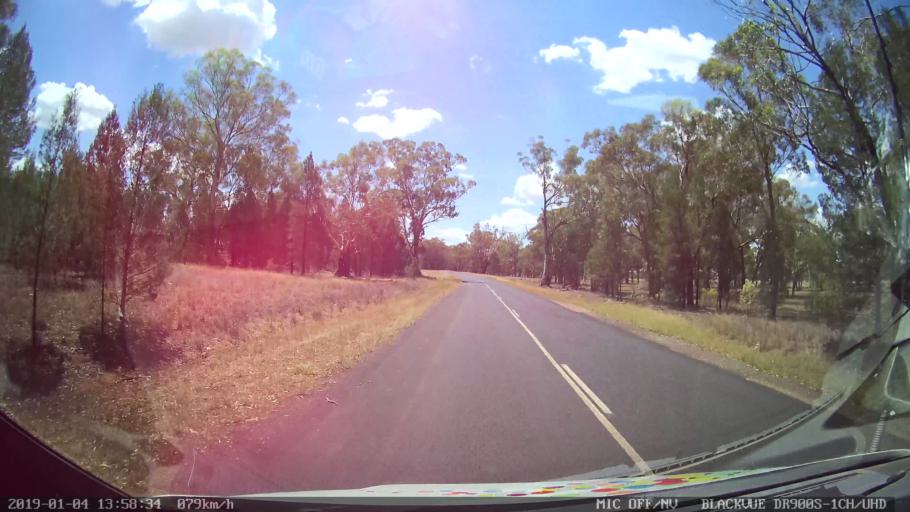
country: AU
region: New South Wales
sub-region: Dubbo Municipality
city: Dubbo
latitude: -32.3271
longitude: 148.5942
